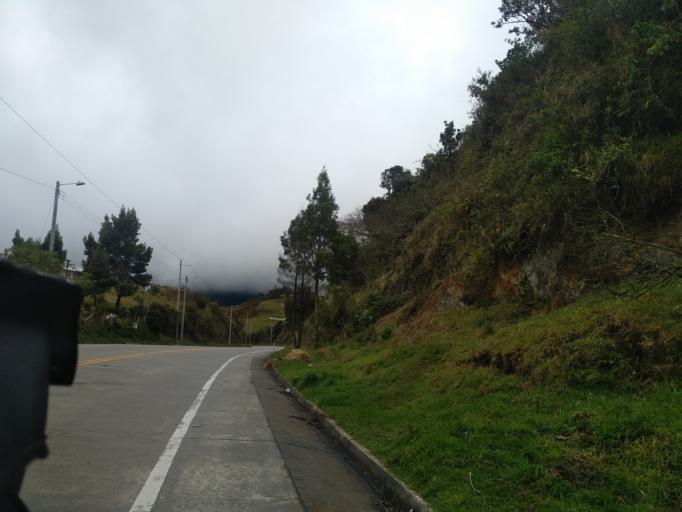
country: EC
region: Loja
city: Catamayo
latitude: -3.8457
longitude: -79.2880
